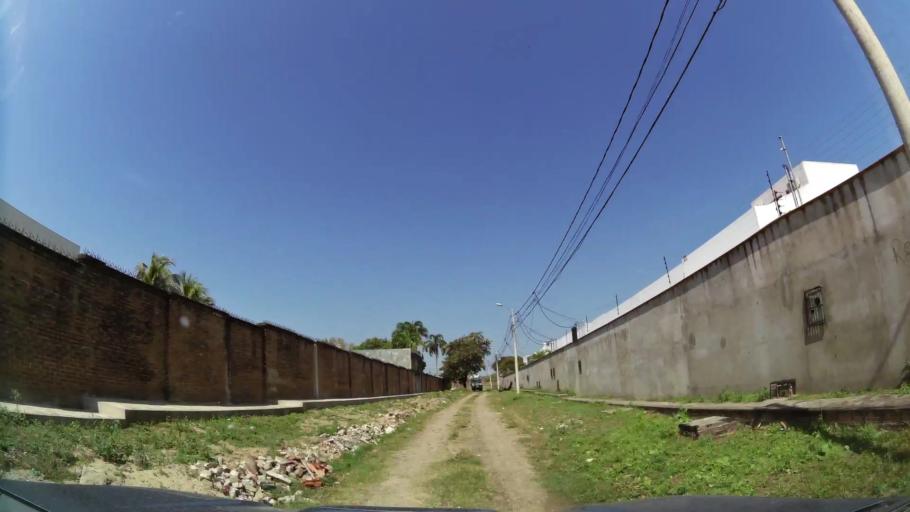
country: BO
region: Santa Cruz
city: Santa Cruz de la Sierra
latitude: -17.7486
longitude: -63.1957
